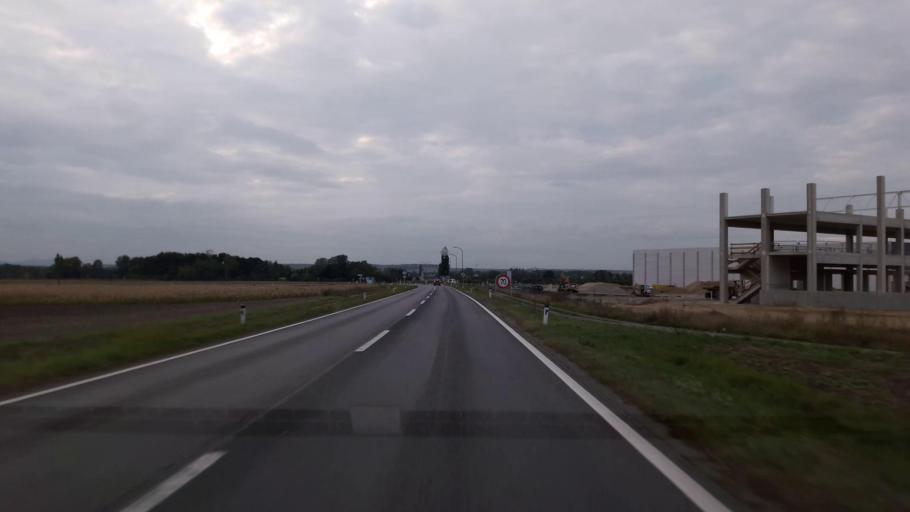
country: AT
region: Lower Austria
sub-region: Politischer Bezirk Bruck an der Leitha
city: Enzersdorf an der Fischa
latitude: 48.0645
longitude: 16.6132
